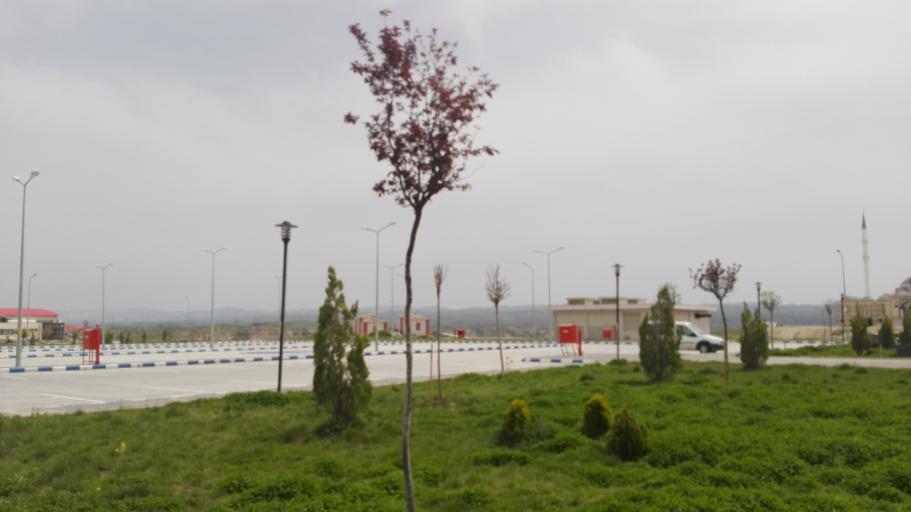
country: TR
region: Batman
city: Oymatas
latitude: 37.7892
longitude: 41.0652
